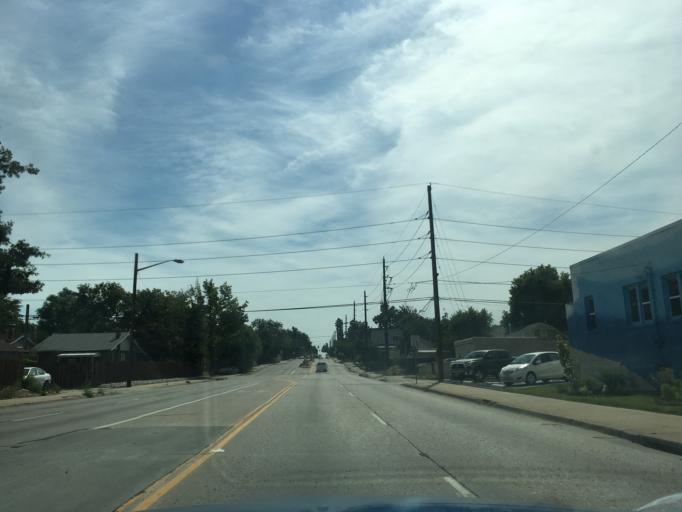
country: US
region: Colorado
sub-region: Arapahoe County
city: Englewood
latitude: 39.6785
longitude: -104.9864
